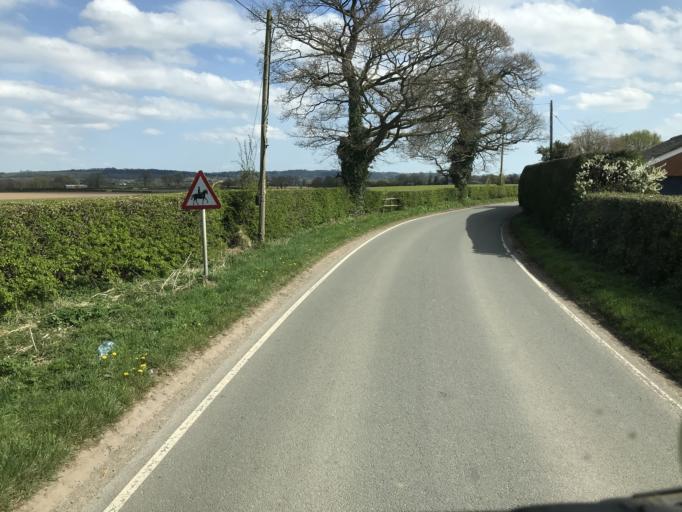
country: GB
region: England
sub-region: Cheshire West and Chester
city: Tarvin
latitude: 53.2114
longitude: -2.7713
